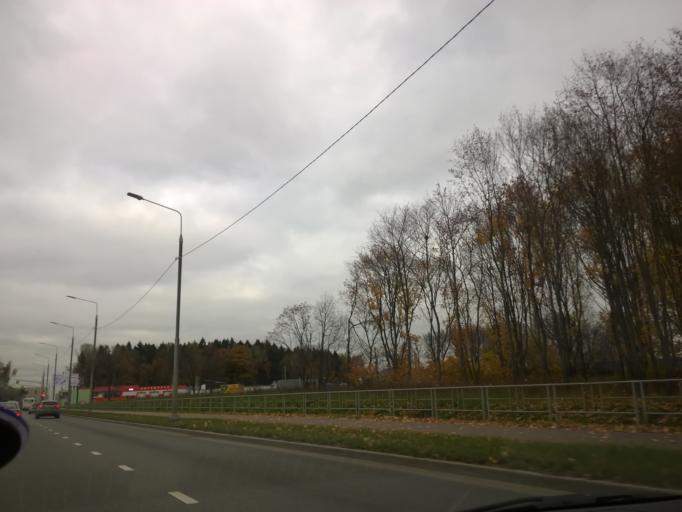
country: RU
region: Moskovskaya
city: Kommunarka
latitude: 55.5574
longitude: 37.4905
